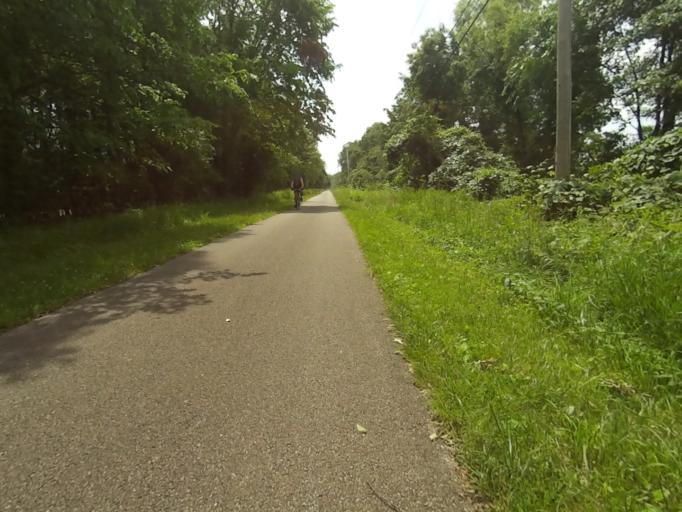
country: US
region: Ohio
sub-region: Summit County
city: Hudson
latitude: 41.2222
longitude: -81.4780
